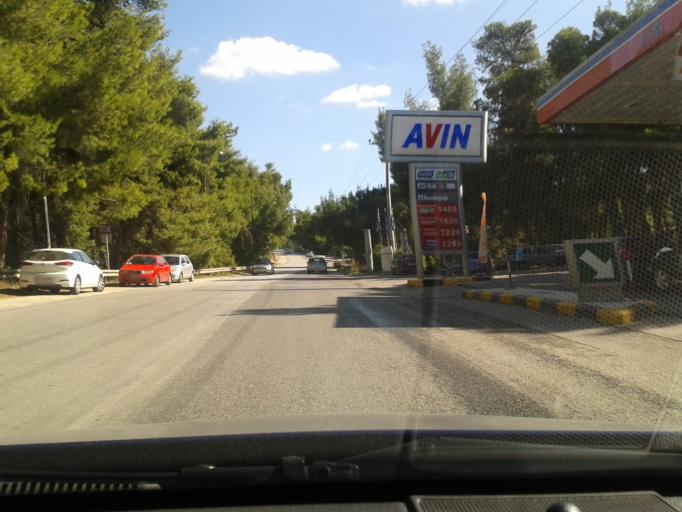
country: GR
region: Attica
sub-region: Nomarchia Anatolikis Attikis
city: Drosia
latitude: 38.1054
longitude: 23.8681
